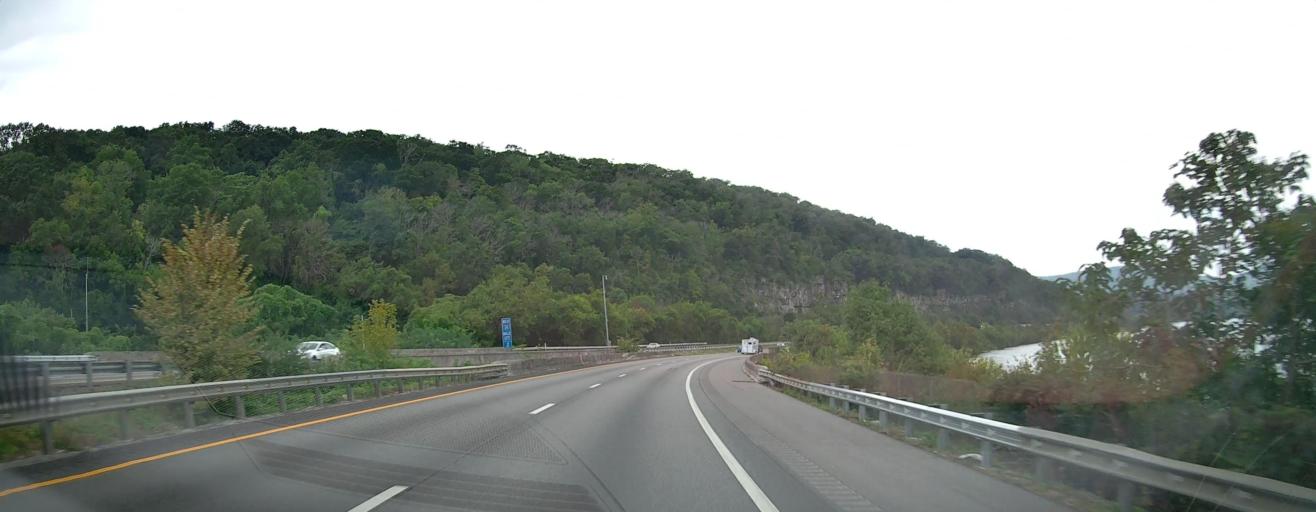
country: US
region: Tennessee
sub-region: Hamilton County
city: Lookout Mountain
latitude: 35.0202
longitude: -85.3330
